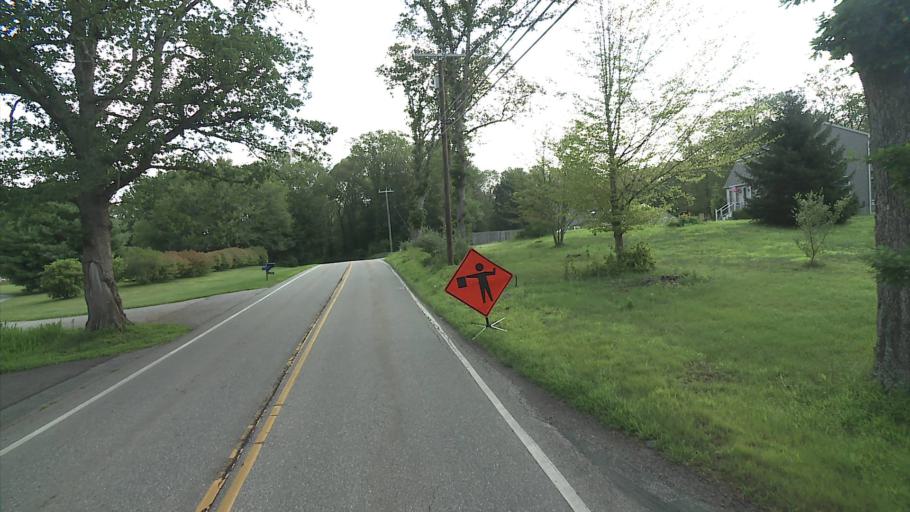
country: US
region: Connecticut
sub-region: Middlesex County
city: Moodus
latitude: 41.5607
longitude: -72.4051
